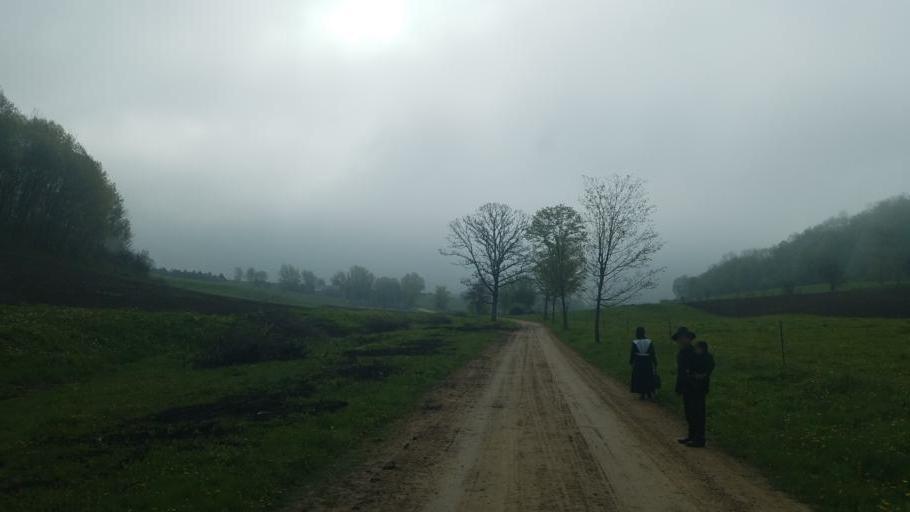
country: US
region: Wisconsin
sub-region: Vernon County
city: Hillsboro
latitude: 43.6244
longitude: -90.3941
